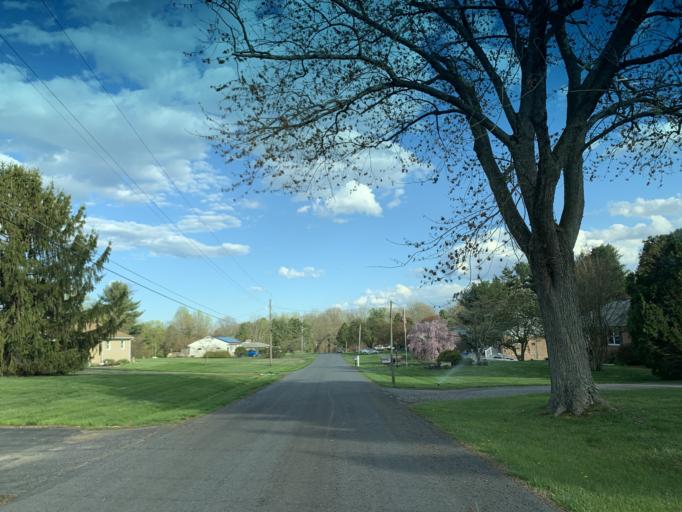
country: US
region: Maryland
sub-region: Harford County
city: South Bel Air
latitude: 39.5941
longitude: -76.3189
